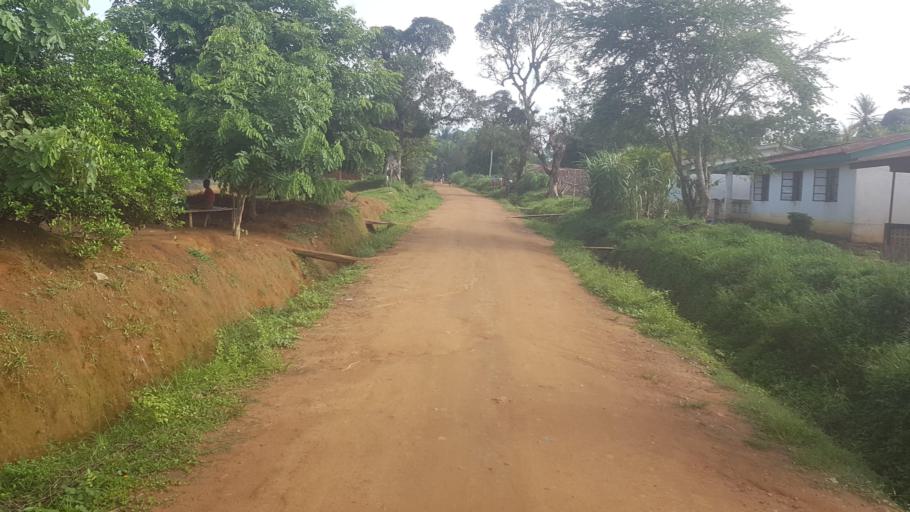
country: SL
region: Southern Province
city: Sumbuya
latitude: 7.6148
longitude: -12.1414
